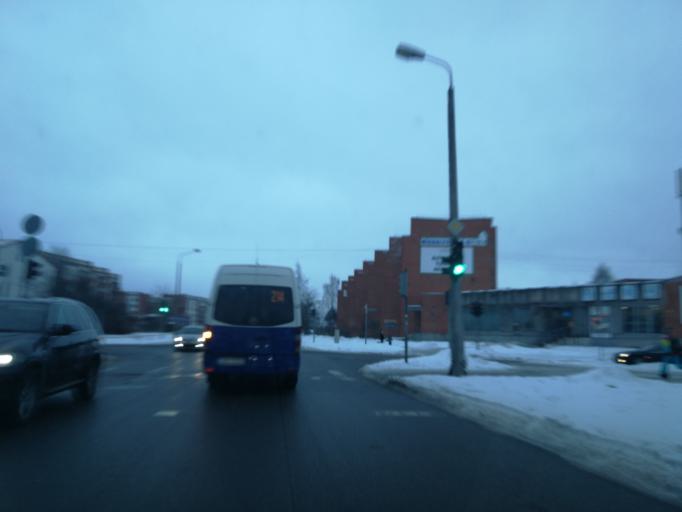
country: LV
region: Riga
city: Riga
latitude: 56.9448
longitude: 24.1725
